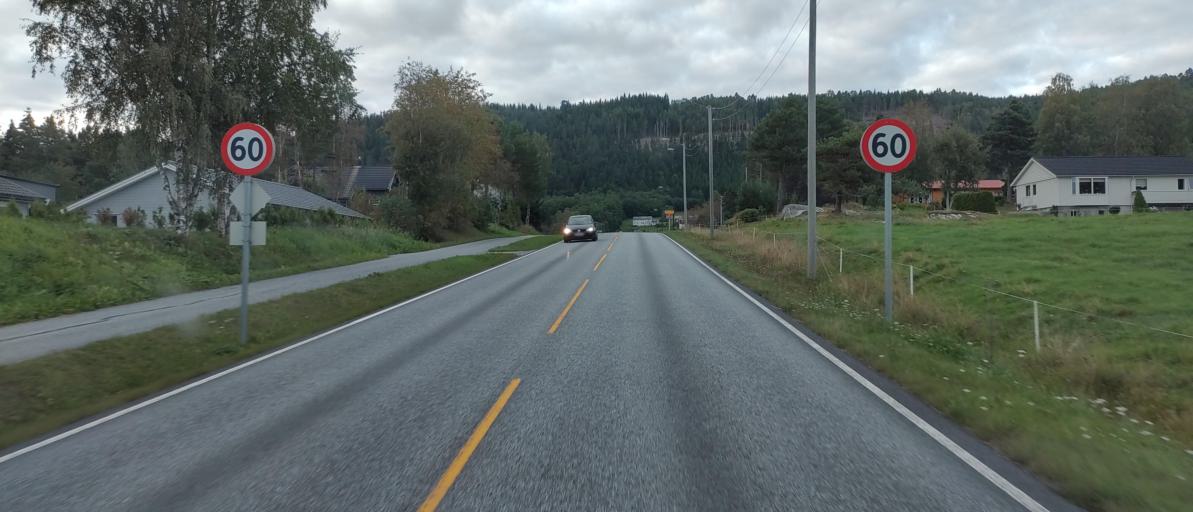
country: NO
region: More og Romsdal
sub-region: Molde
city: Hjelset
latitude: 62.7302
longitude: 7.4236
